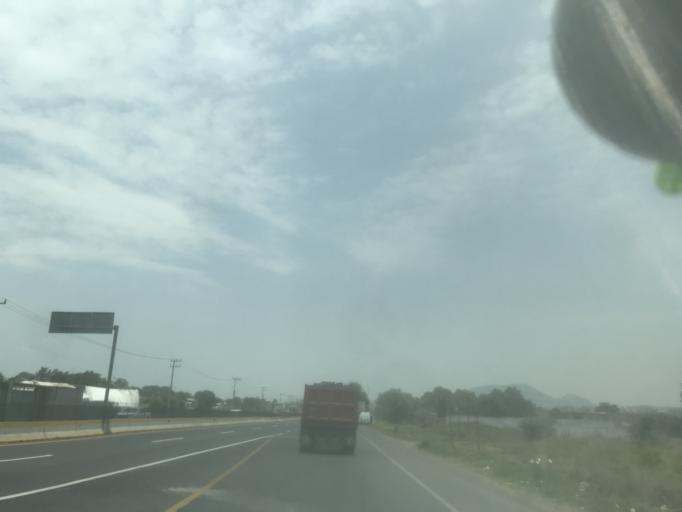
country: MX
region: Mexico
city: Amecameca de Juarez
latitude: 19.1271
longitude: -98.7805
